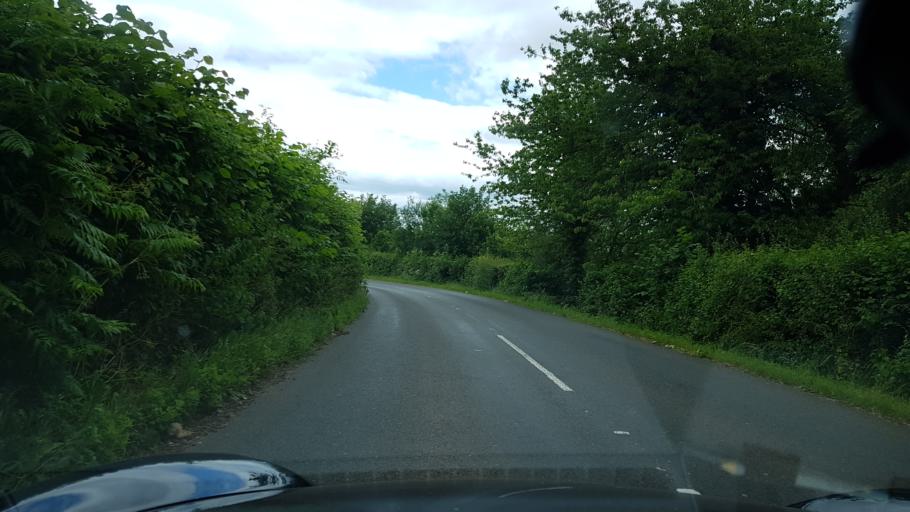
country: GB
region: Wales
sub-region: Monmouthshire
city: Grosmont
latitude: 51.8727
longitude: -2.8610
